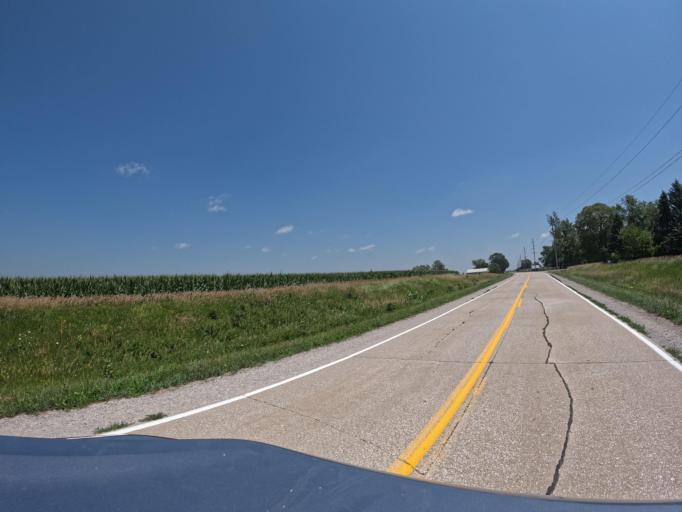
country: US
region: Iowa
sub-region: Keokuk County
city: Sigourney
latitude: 41.2757
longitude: -92.1689
